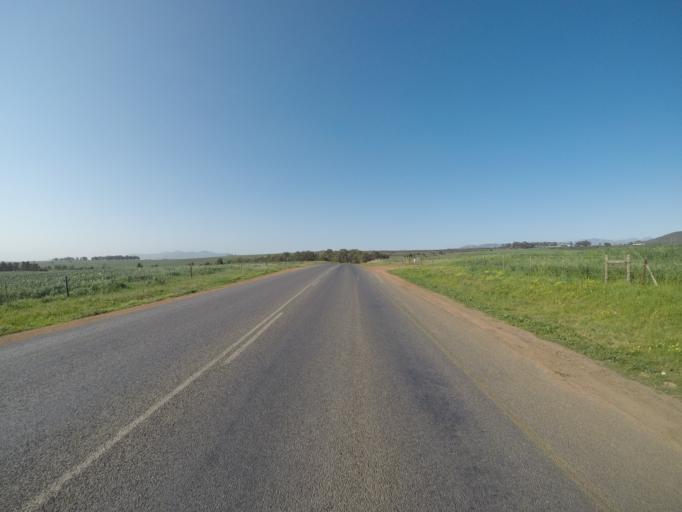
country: ZA
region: Western Cape
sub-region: City of Cape Town
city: Kraaifontein
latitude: -33.7673
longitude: 18.7586
